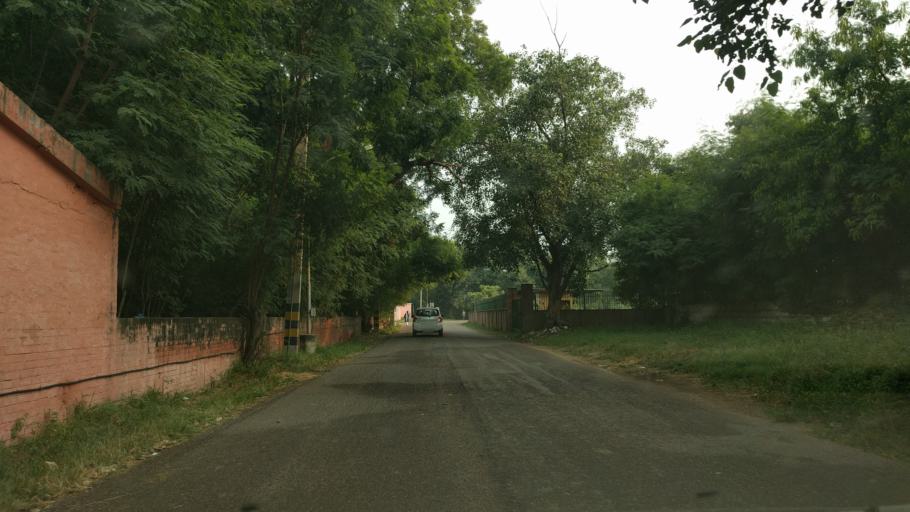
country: IN
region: NCT
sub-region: Central Delhi
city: Karol Bagh
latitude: 28.6286
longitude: 77.1527
